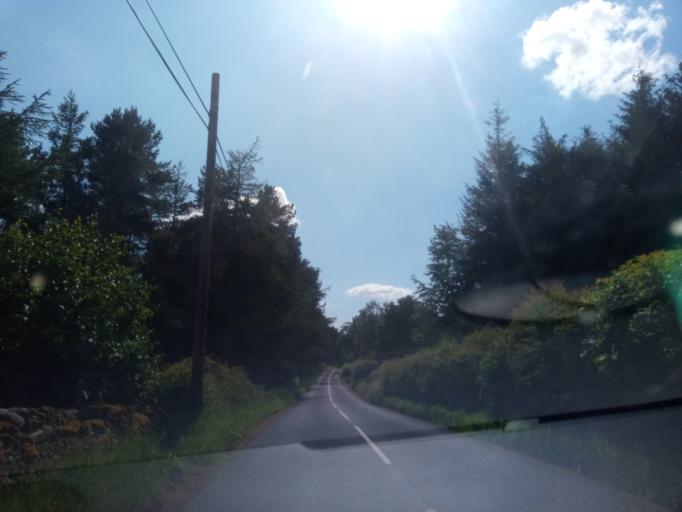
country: GB
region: Scotland
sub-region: The Scottish Borders
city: Innerleithen
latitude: 55.5225
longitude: -3.0434
